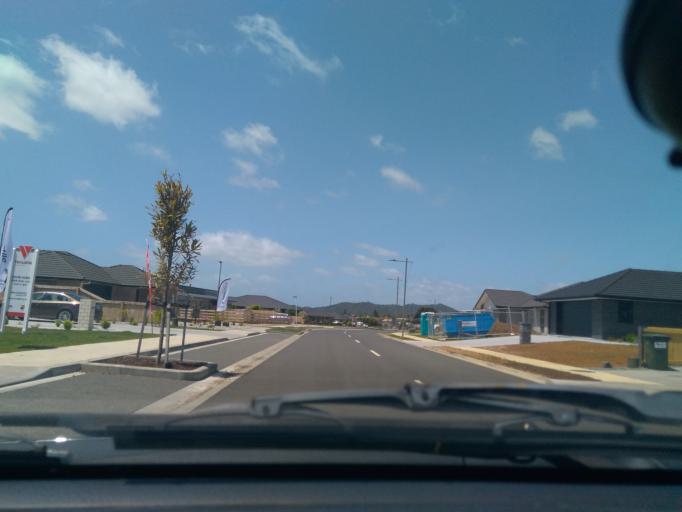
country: NZ
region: Northland
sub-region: Whangarei
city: Whangarei
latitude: -35.6739
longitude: 174.3163
